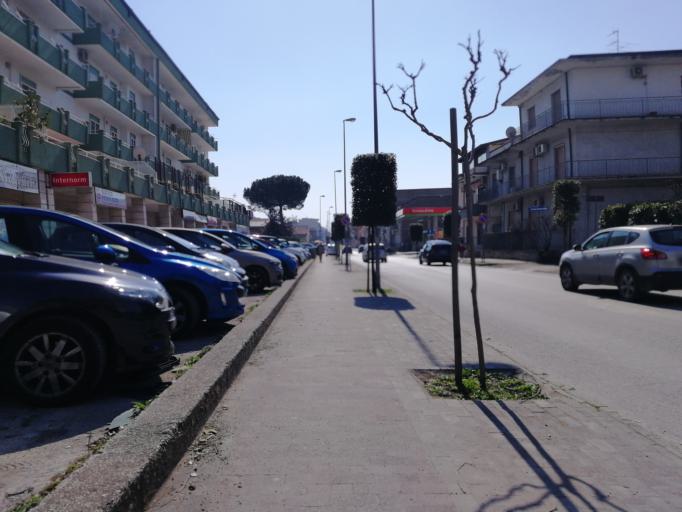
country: IT
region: Campania
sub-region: Provincia di Caserta
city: Santa Maria Capua Vetere
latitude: 41.0894
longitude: 14.2536
